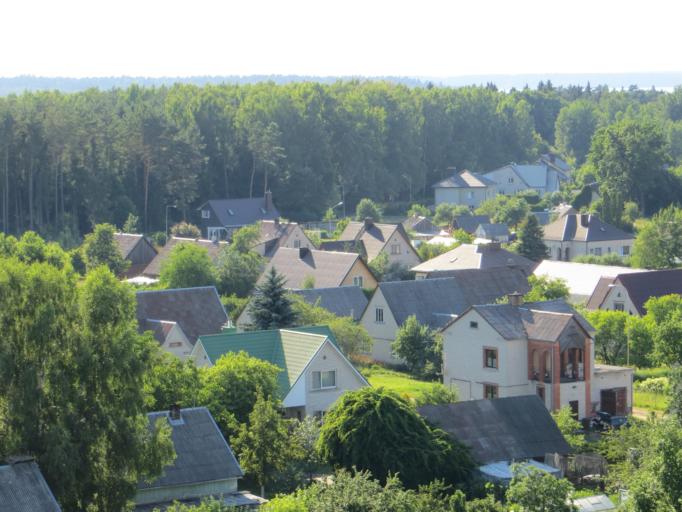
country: LT
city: Ziezmariai
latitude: 54.8290
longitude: 24.2466
